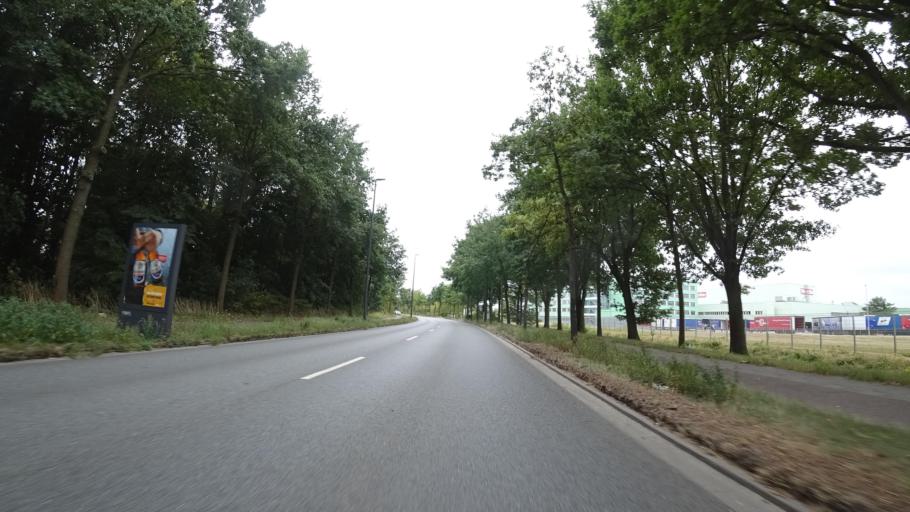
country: DE
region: North Rhine-Westphalia
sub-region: Regierungsbezirk Detmold
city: Guetersloh
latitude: 51.9146
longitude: 8.4067
